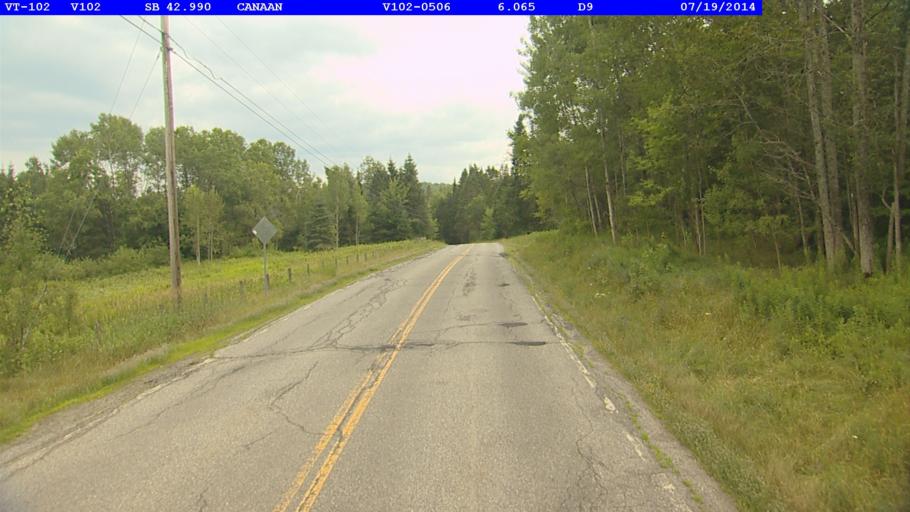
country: US
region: New Hampshire
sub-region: Coos County
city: Colebrook
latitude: 44.9860
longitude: -71.5425
